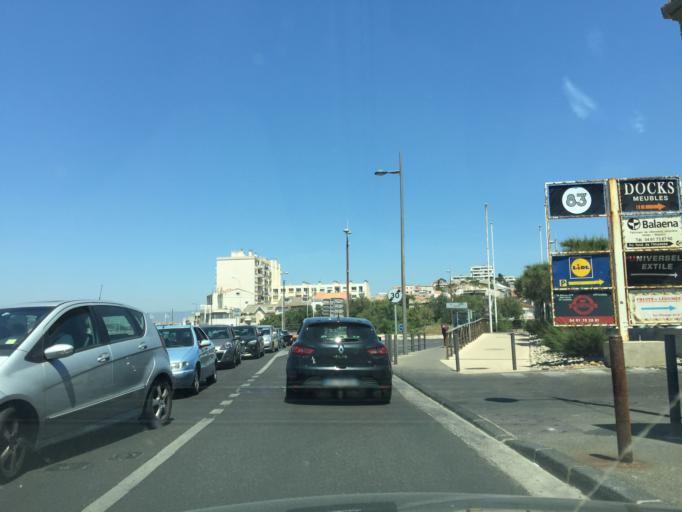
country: FR
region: Provence-Alpes-Cote d'Azur
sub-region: Departement des Bouches-du-Rhone
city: Marseille 08
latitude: 43.2456
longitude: 5.3733
